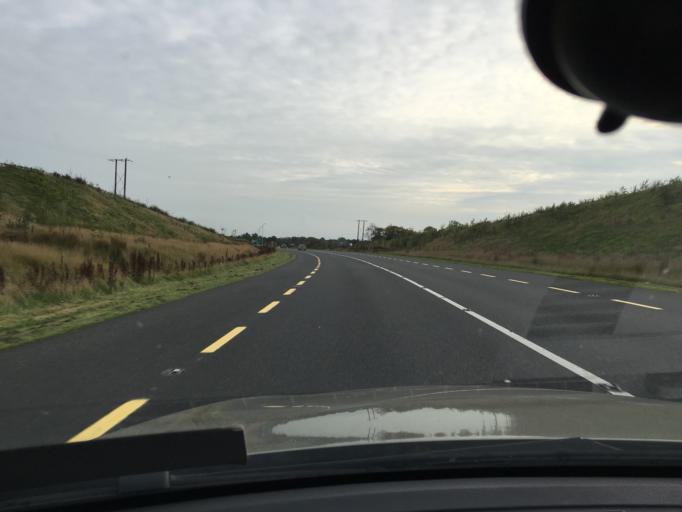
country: IE
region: Leinster
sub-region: An Longfort
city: Longford
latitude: 53.7287
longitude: -7.8253
